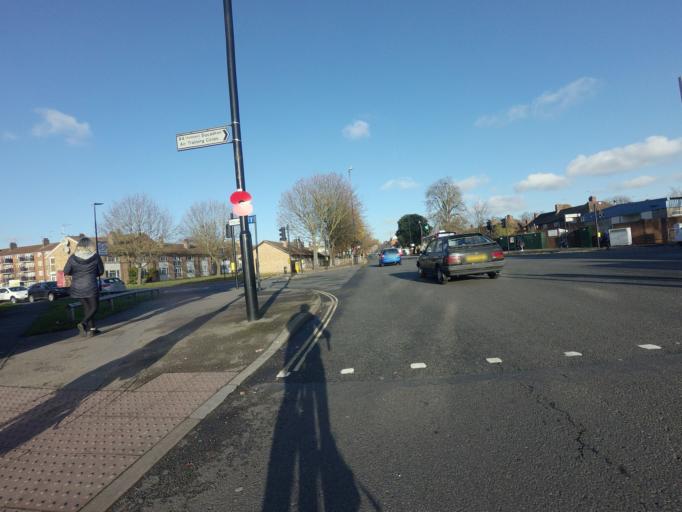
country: GB
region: England
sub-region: Greater London
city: Feltham
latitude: 51.4409
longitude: -0.4147
